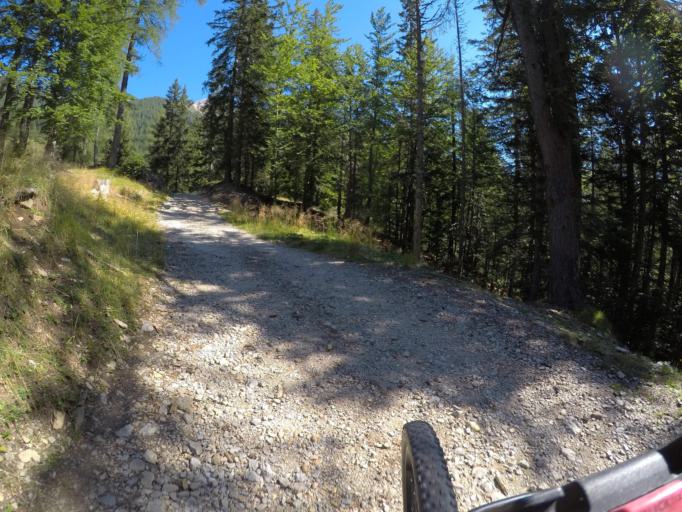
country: IT
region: Friuli Venezia Giulia
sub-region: Provincia di Udine
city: Malborghetto
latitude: 46.4610
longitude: 13.4500
